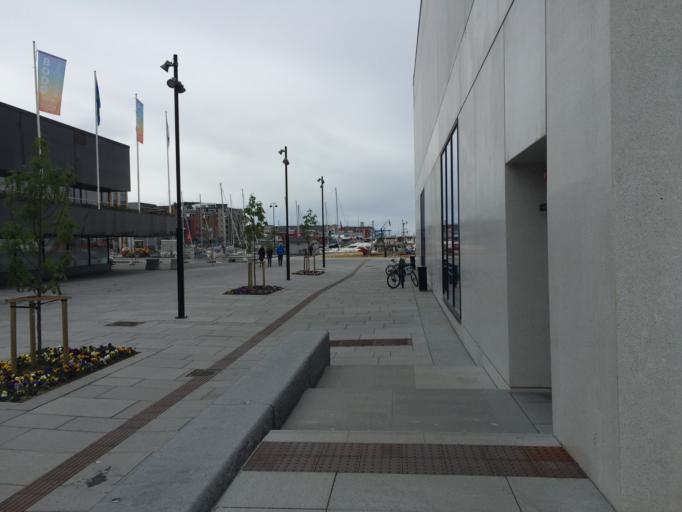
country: NO
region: Nordland
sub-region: Bodo
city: Bodo
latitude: 67.2826
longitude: 14.3745
